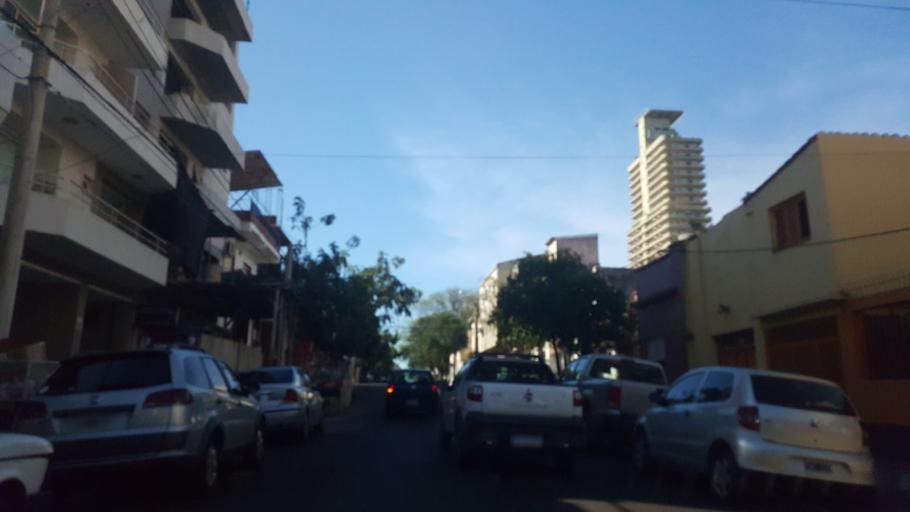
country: AR
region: Misiones
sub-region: Departamento de Capital
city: Posadas
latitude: -27.3644
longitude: -55.8900
